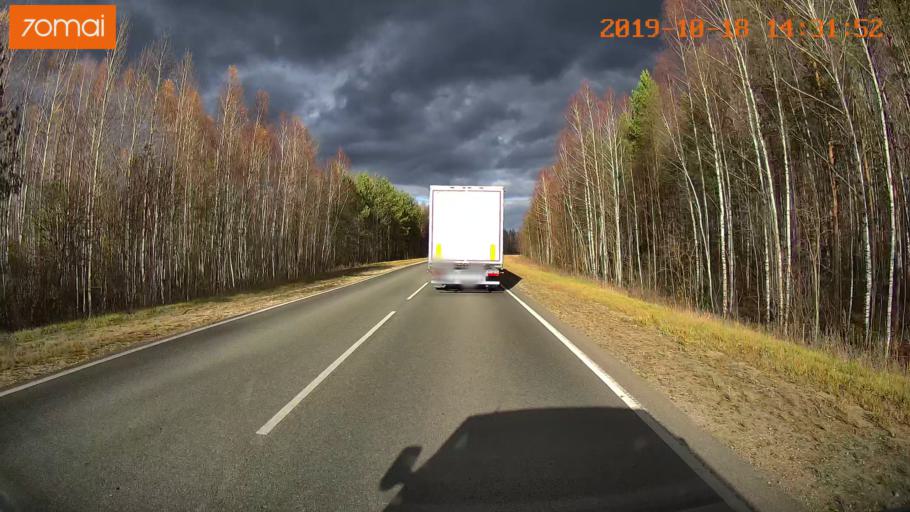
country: RU
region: Rjazan
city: Tuma
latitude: 55.1866
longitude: 40.5730
